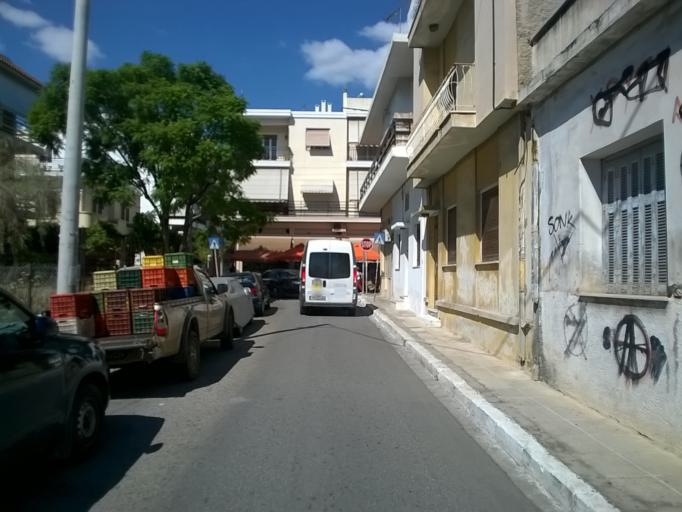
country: GR
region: Attica
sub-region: Nomos Piraios
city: Nikaia
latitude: 37.9635
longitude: 23.6536
